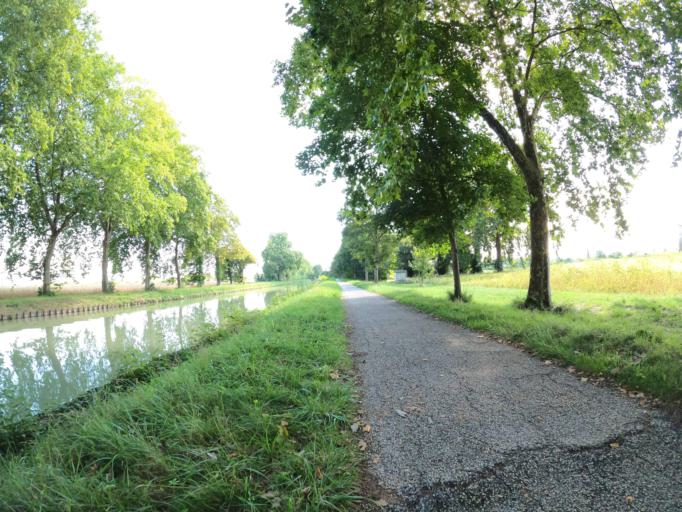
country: FR
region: Midi-Pyrenees
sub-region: Departement du Tarn-et-Garonne
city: Lamagistere
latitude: 44.1206
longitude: 0.8470
